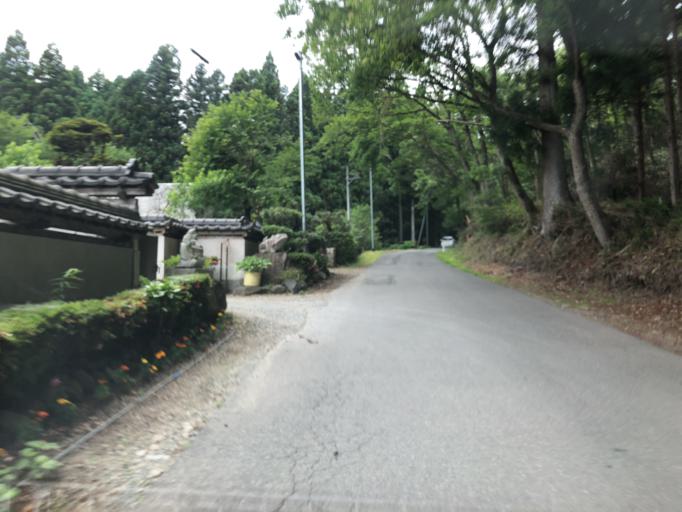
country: JP
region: Miyagi
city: Marumori
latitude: 37.8274
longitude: 140.8677
